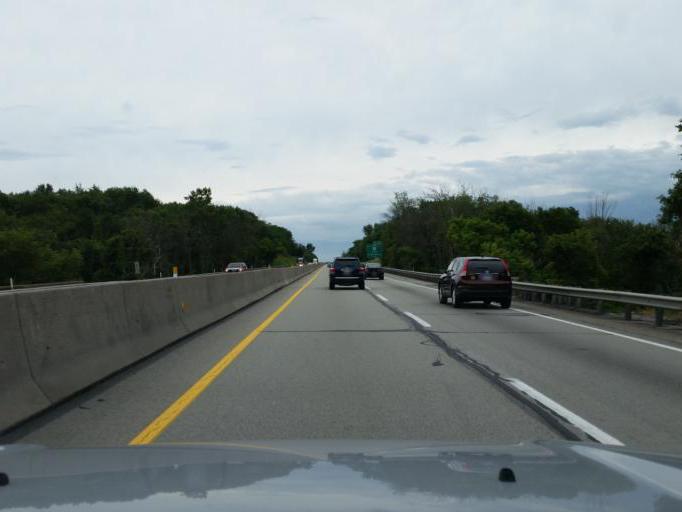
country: US
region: Pennsylvania
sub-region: Westmoreland County
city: Irwin
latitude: 40.3276
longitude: -79.6858
